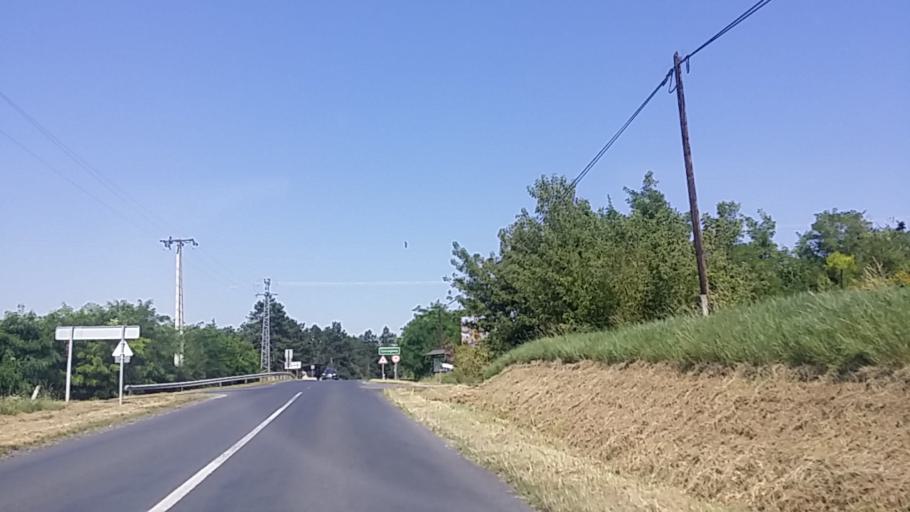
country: HU
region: Zala
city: Cserszegtomaj
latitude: 46.7972
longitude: 17.2076
